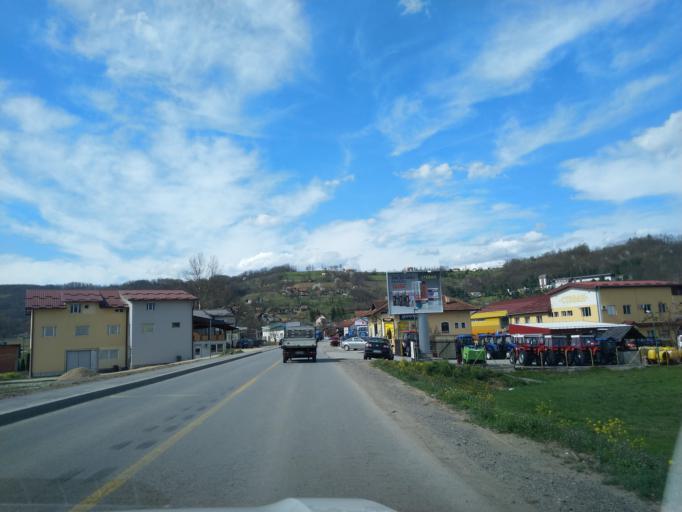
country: RS
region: Central Serbia
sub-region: Zlatiborski Okrug
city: Arilje
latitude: 43.7618
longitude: 20.0959
